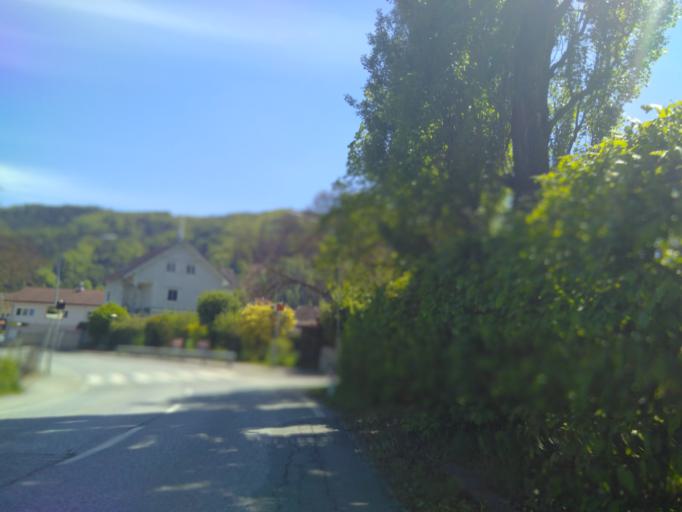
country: AT
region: Styria
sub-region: Politischer Bezirk Graz-Umgebung
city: Gratkorn
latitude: 47.1175
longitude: 15.3400
